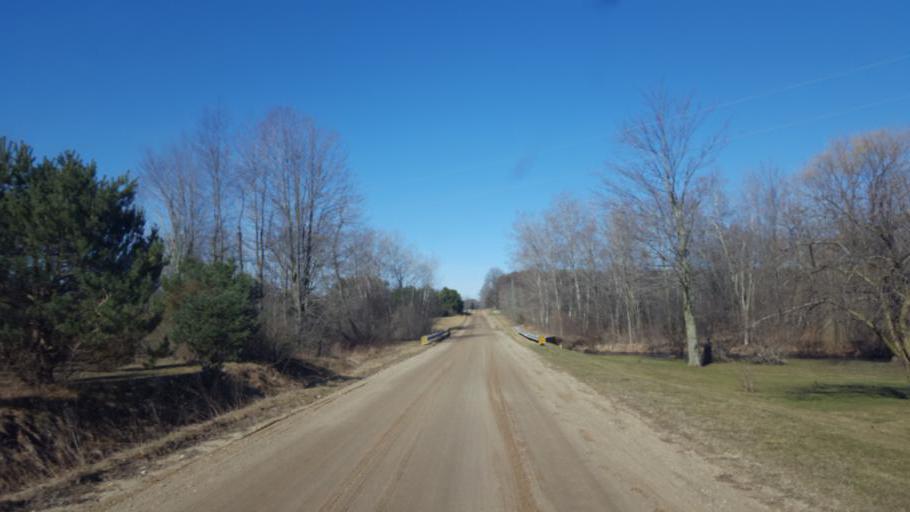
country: US
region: Michigan
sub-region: Isabella County
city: Lake Isabella
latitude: 43.5383
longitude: -85.0067
